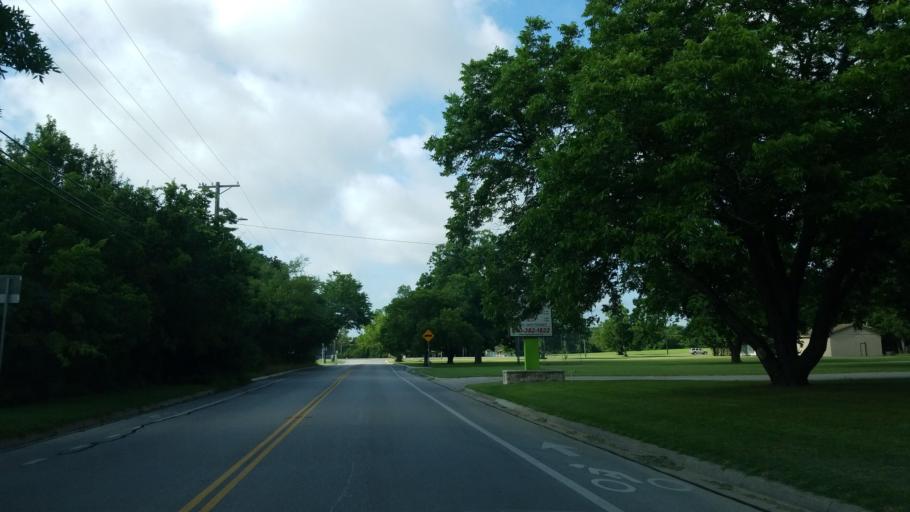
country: US
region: Texas
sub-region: Denton County
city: Denton
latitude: 33.2156
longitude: -97.0965
